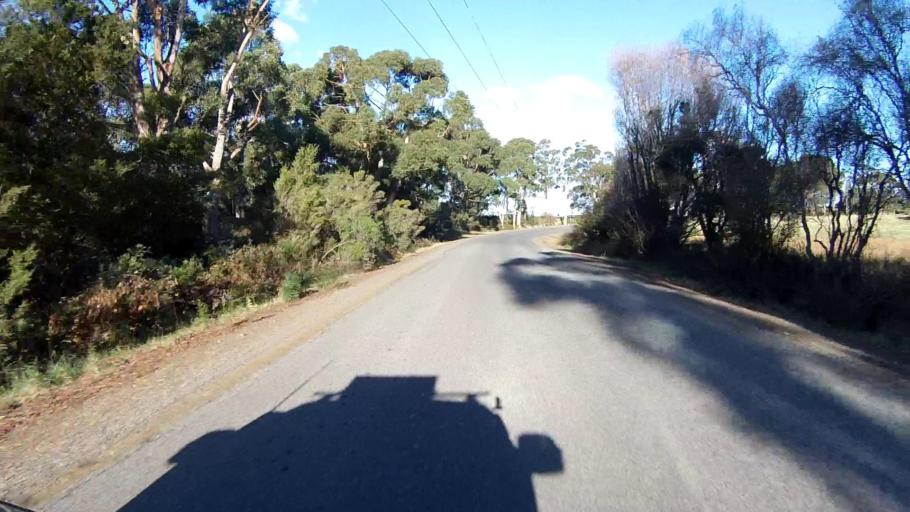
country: AU
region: Tasmania
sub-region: Clarence
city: Sandford
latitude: -43.1658
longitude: 147.8594
